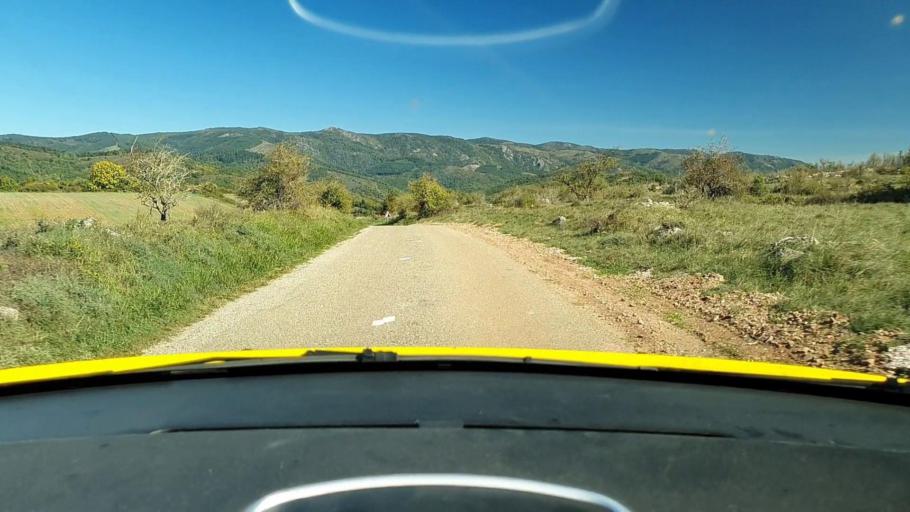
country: FR
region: Languedoc-Roussillon
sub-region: Departement du Gard
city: Aveze
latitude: 43.9587
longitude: 3.4242
